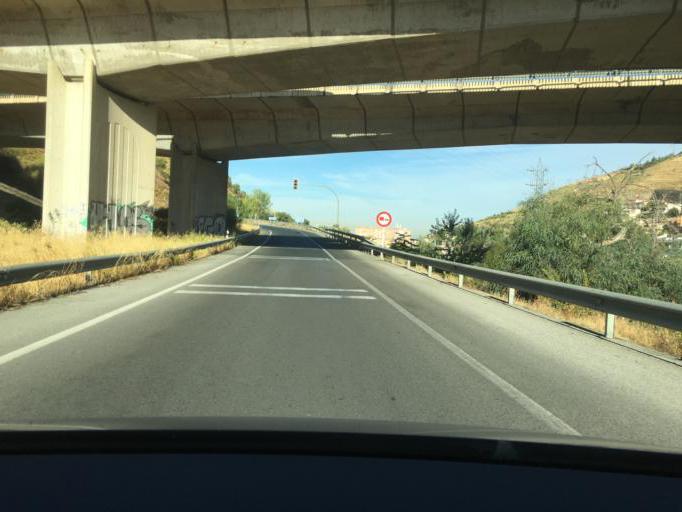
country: ES
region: Andalusia
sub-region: Provincia de Granada
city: Huetor Vega
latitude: 37.1616
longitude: -3.5711
